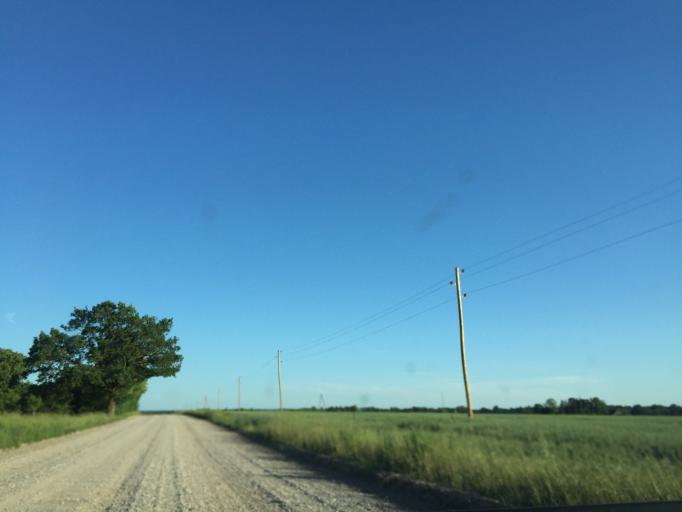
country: LV
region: Broceni
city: Broceni
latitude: 56.8033
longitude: 22.5482
